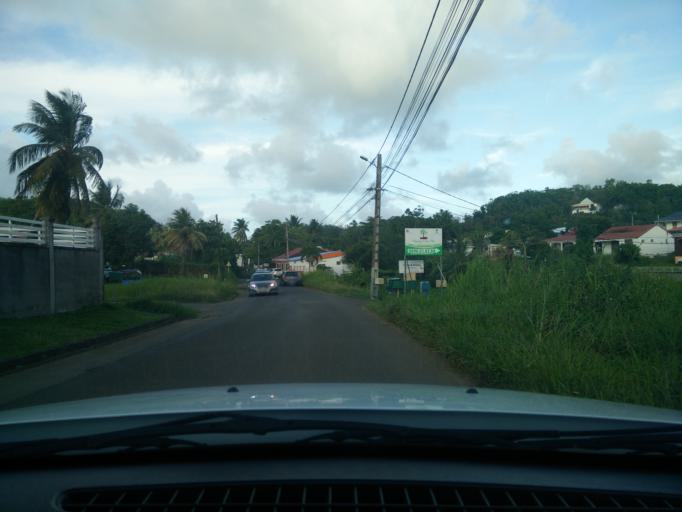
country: GP
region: Guadeloupe
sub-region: Guadeloupe
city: Les Abymes
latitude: 16.2545
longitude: -61.5029
